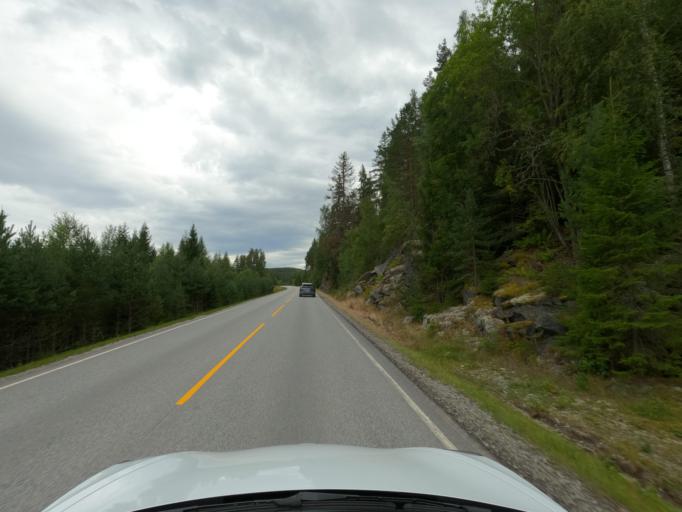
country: NO
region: Telemark
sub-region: Hjartdal
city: Sauland
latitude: 59.7062
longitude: 9.0122
